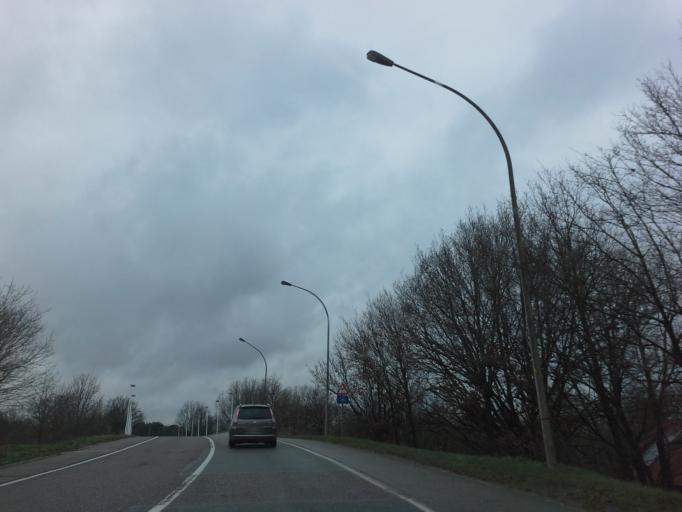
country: BE
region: Flanders
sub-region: Provincie Antwerpen
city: Balen
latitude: 51.1538
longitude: 5.1490
